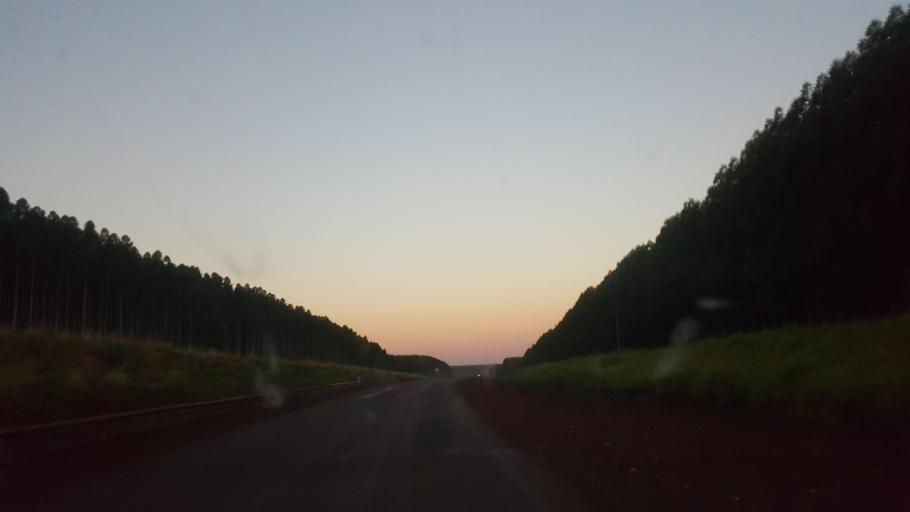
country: AR
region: Corrientes
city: Garruchos
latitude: -28.2479
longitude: -55.8427
